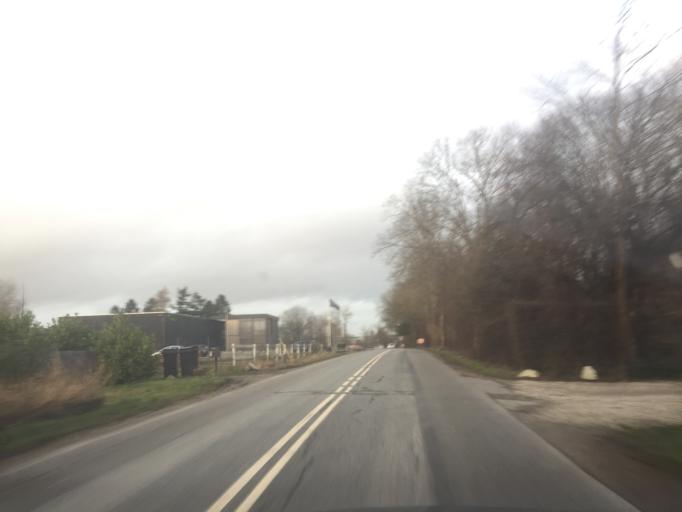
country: DK
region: Capital Region
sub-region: Egedal Kommune
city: Smorumnedre
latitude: 55.7046
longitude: 12.3242
